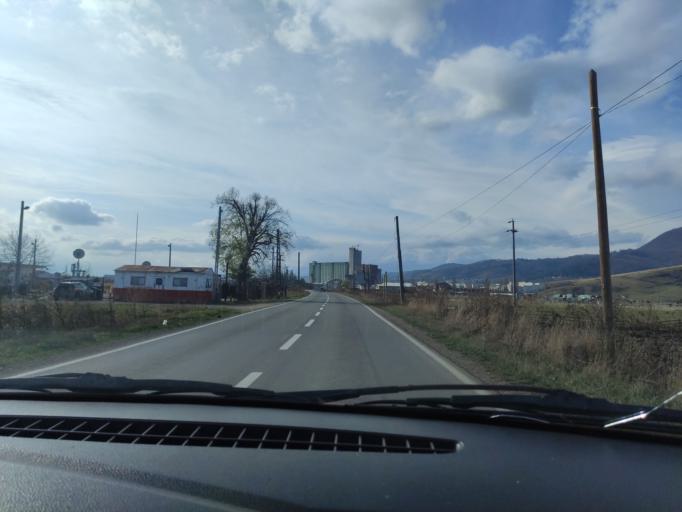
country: RO
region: Brasov
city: Codlea
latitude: 45.7126
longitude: 25.4651
